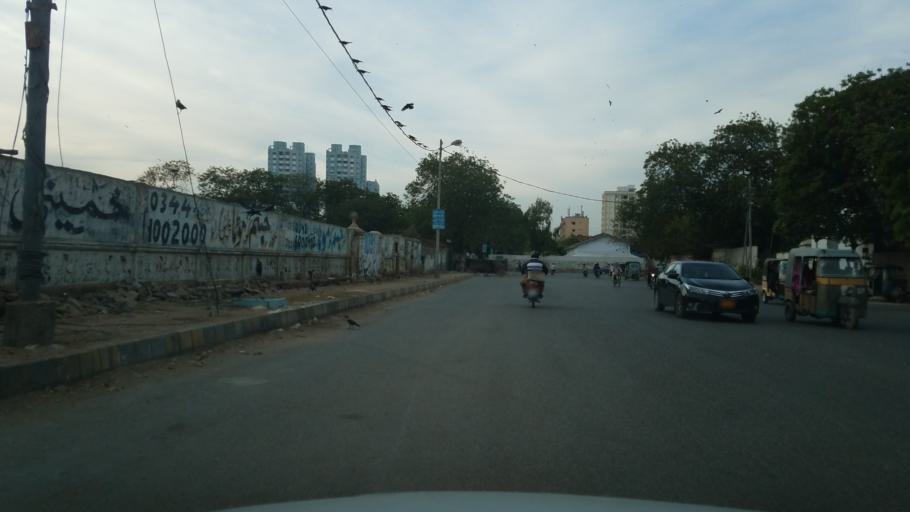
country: PK
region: Sindh
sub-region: Karachi District
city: Karachi
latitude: 24.8678
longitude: 67.0277
